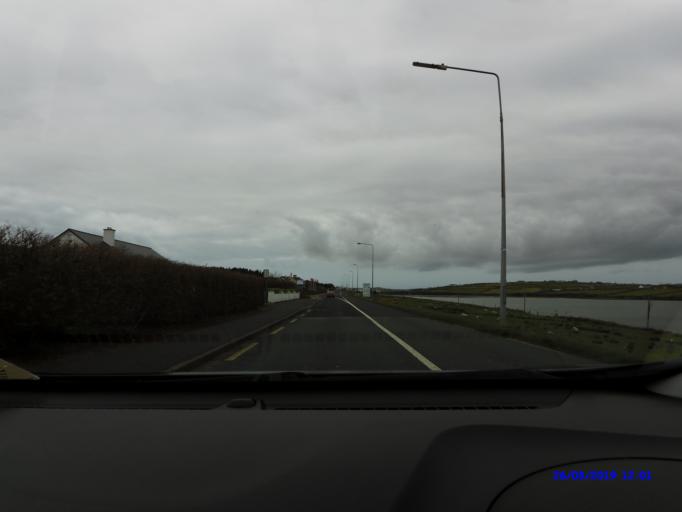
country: IE
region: Connaught
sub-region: Maigh Eo
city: Belmullet
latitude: 54.2184
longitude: -9.9742
